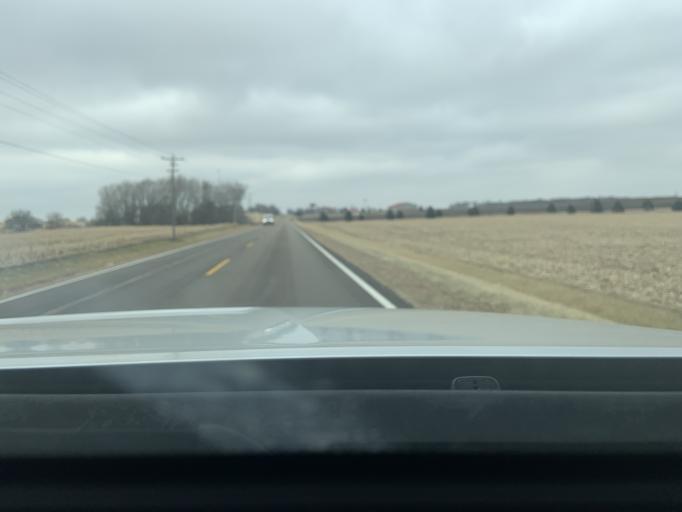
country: US
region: Illinois
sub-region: LaSalle County
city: Seneca
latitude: 41.3847
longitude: -88.6134
